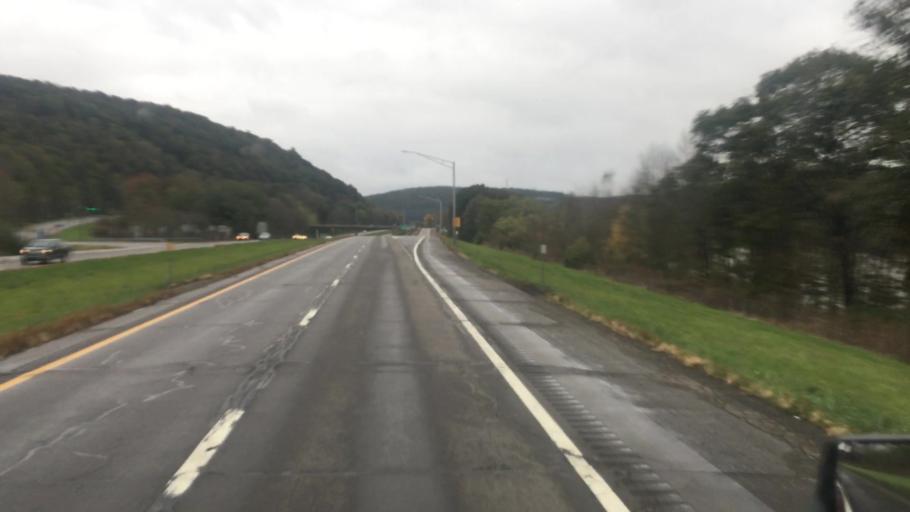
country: US
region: New York
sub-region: Tioga County
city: Owego
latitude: 42.0869
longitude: -76.2262
